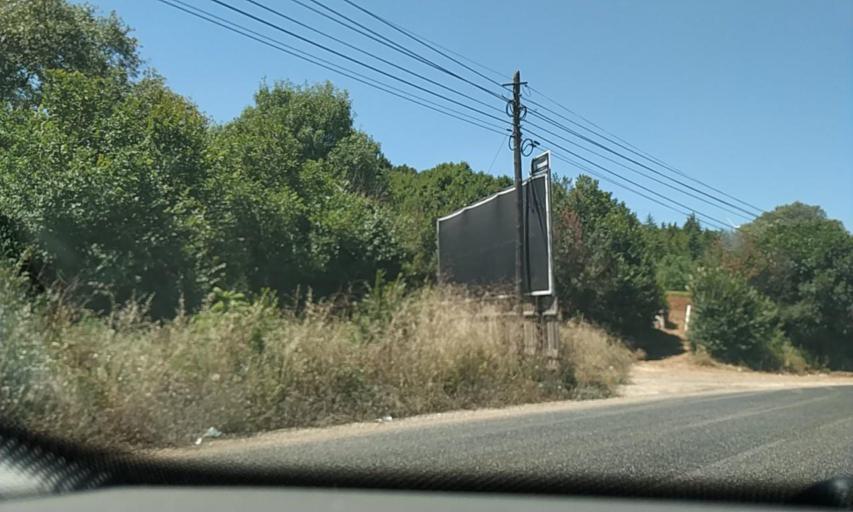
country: PT
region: Lisbon
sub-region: Odivelas
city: Canecas
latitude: 38.8623
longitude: -9.2102
